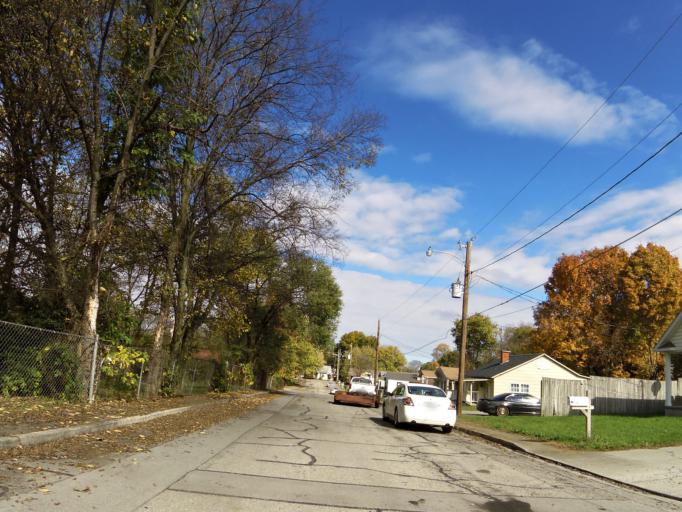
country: US
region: Tennessee
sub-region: Blount County
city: Maryville
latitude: 35.7689
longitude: -83.9661
